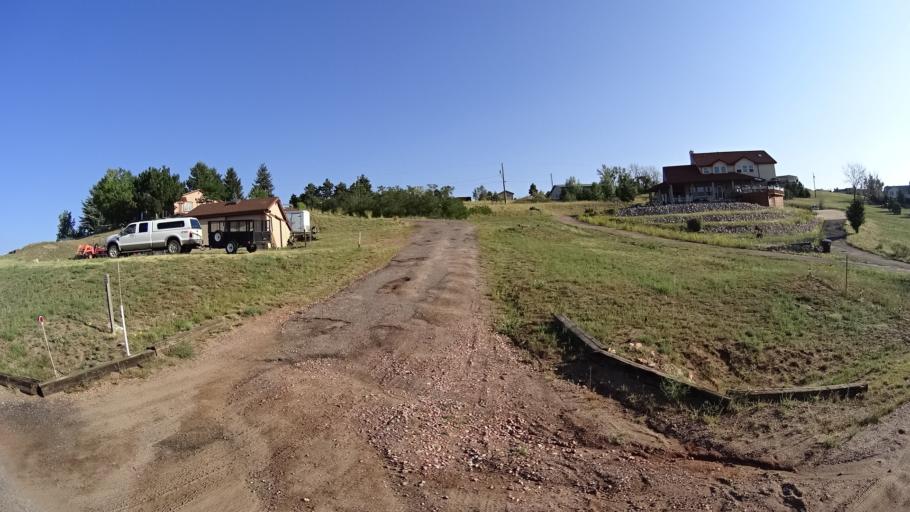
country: US
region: Colorado
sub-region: El Paso County
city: Black Forest
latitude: 38.9369
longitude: -104.7718
